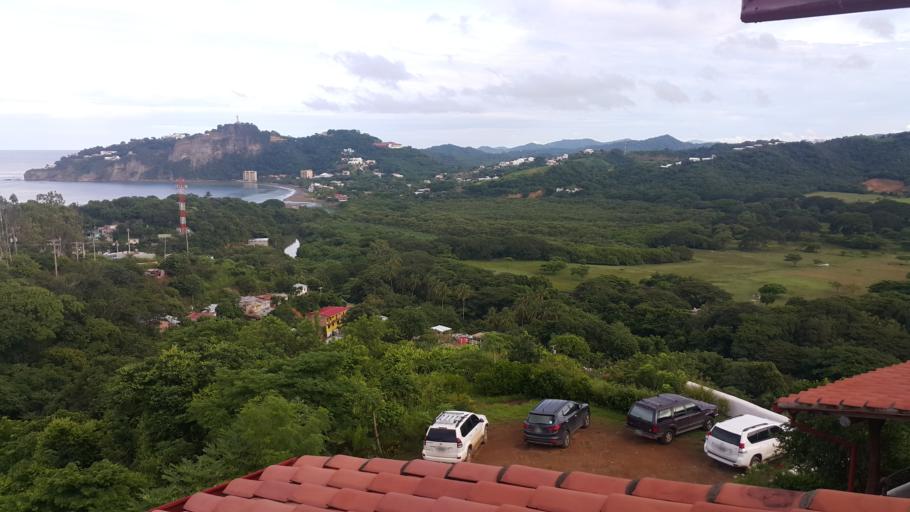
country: NI
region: Rivas
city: San Juan del Sur
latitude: 11.2555
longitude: -85.8655
